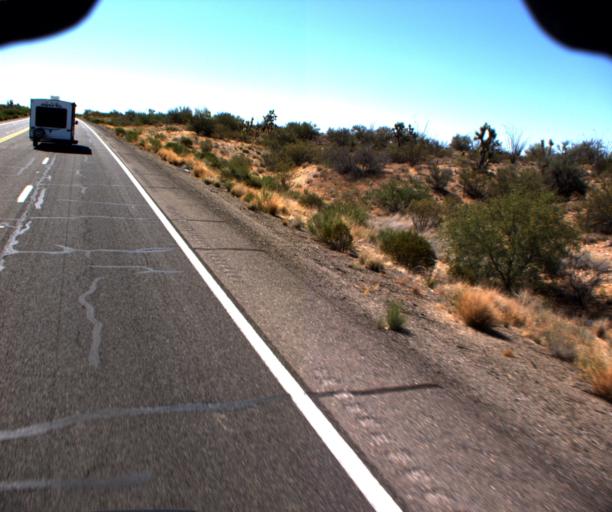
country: US
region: Arizona
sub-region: Yavapai County
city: Congress
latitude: 34.1909
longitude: -113.0532
